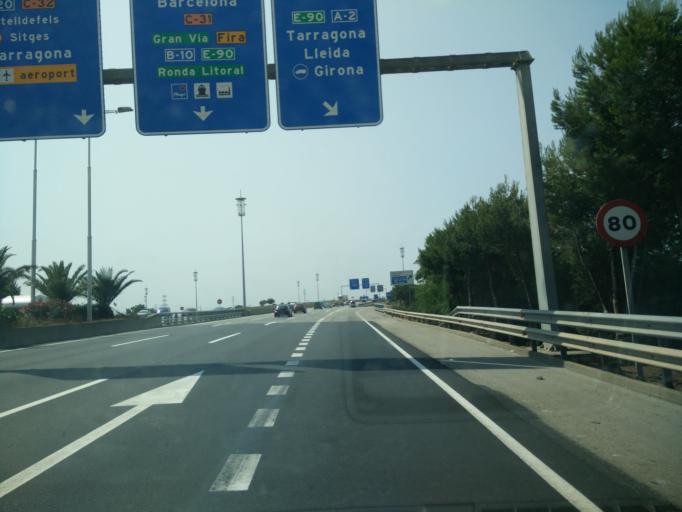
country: ES
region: Catalonia
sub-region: Provincia de Barcelona
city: Cornella de Llobregat
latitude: 41.3486
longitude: 2.0921
